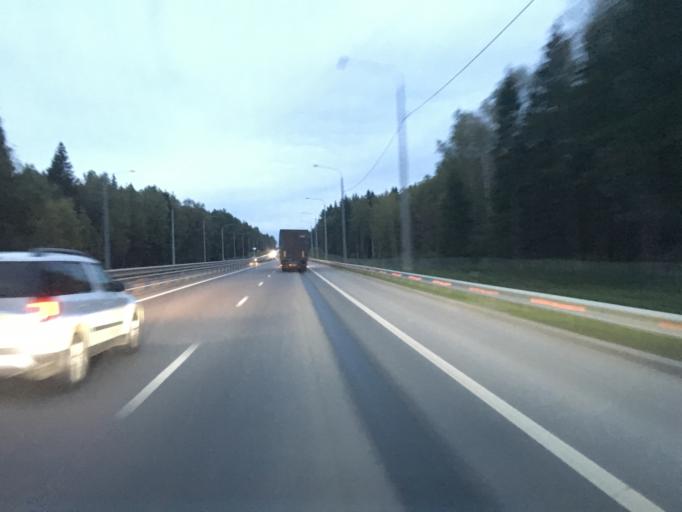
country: RU
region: Kaluga
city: Maloyaroslavets
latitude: 54.9328
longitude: 36.4179
